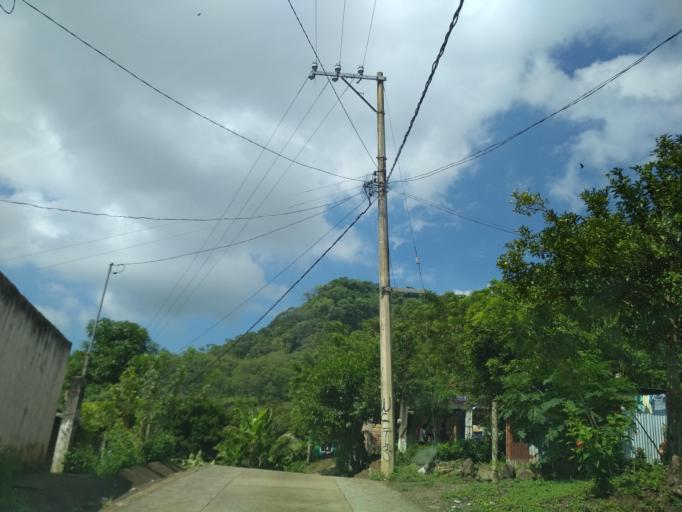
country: MX
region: Veracruz
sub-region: San Andres Tuxtla
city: Texcaltitan Xoteapan (Texcaltitan)
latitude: 18.4486
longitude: -95.2545
